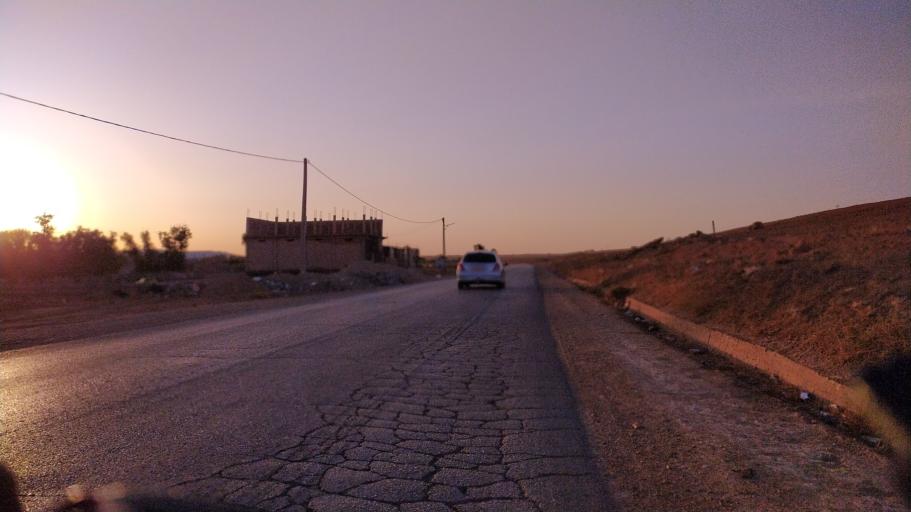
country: DZ
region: Tiaret
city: Frenda
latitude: 34.9002
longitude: 1.2443
